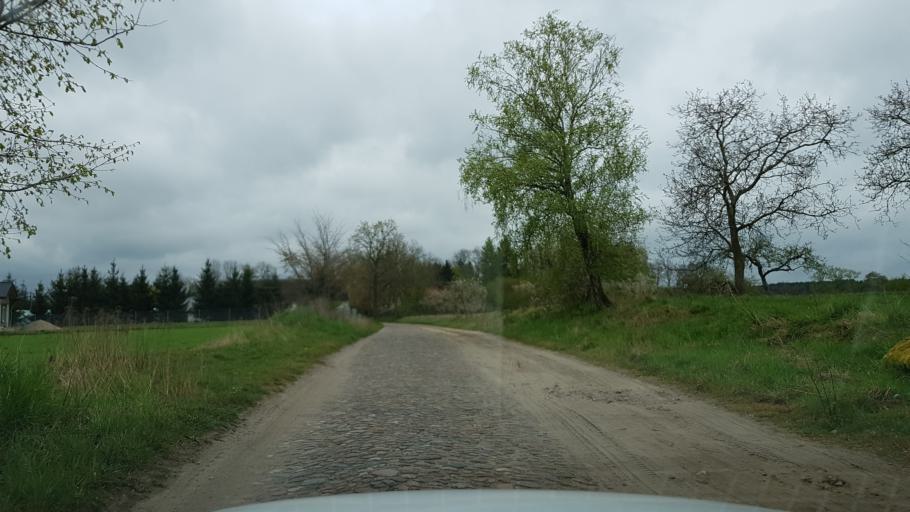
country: PL
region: West Pomeranian Voivodeship
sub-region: Powiat kolobrzeski
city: Ryman
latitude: 54.0318
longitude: 15.5244
